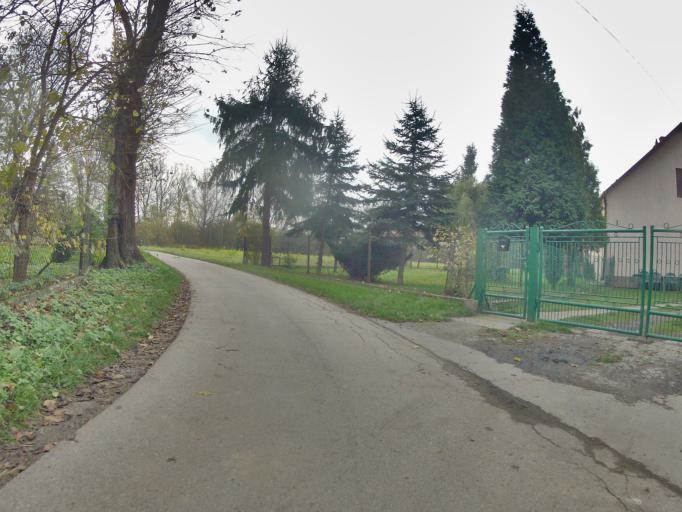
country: PL
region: Lesser Poland Voivodeship
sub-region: Powiat wielicki
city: Wegrzce Wielkie
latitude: 50.0490
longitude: 20.1141
